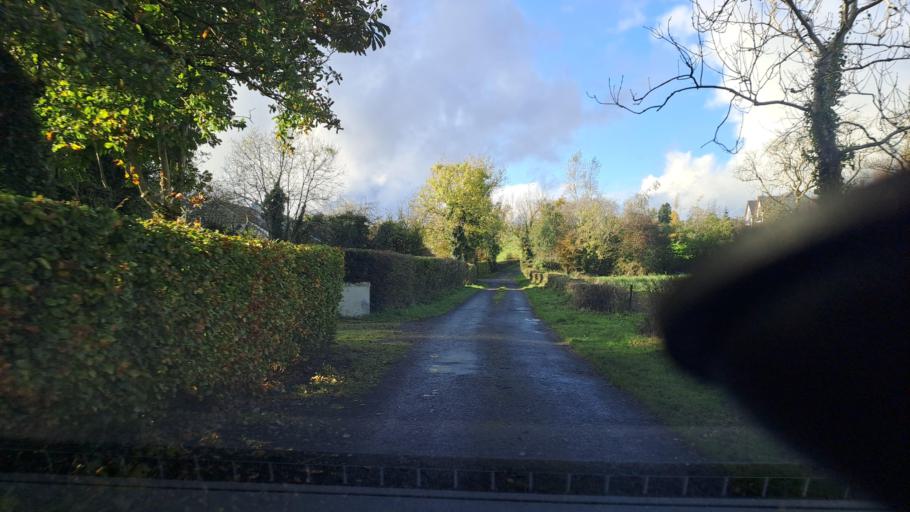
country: IE
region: Ulster
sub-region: An Cabhan
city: Bailieborough
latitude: 53.9349
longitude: -6.9486
